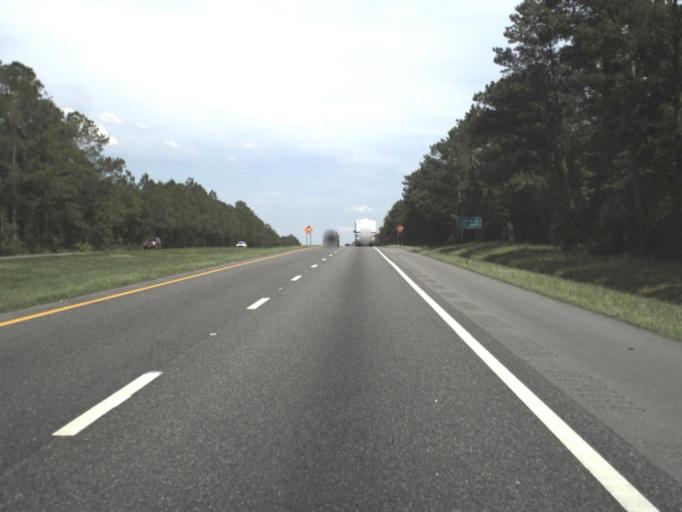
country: US
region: Florida
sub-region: Columbia County
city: Five Points
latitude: 30.2487
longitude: -82.7030
